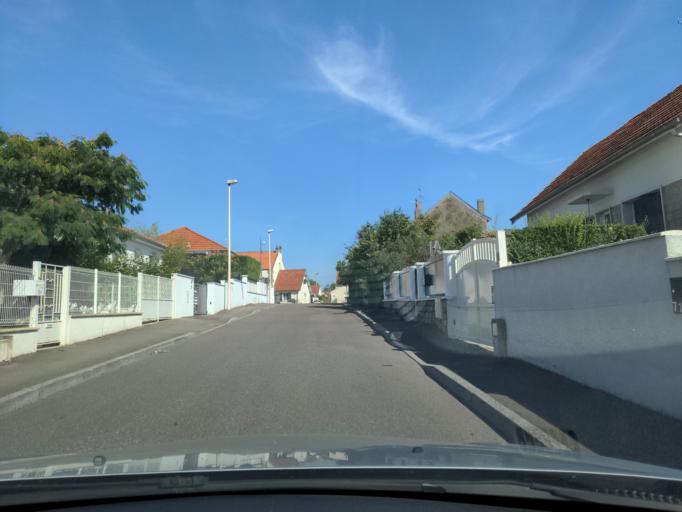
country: FR
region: Bourgogne
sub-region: Departement de la Cote-d'Or
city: Saint-Apollinaire
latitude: 47.3304
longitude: 5.0822
